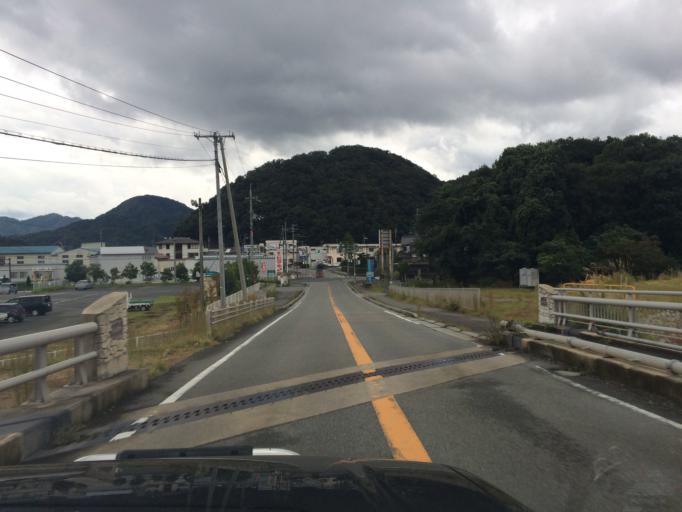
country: JP
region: Hyogo
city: Toyooka
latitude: 35.4572
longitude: 134.7726
